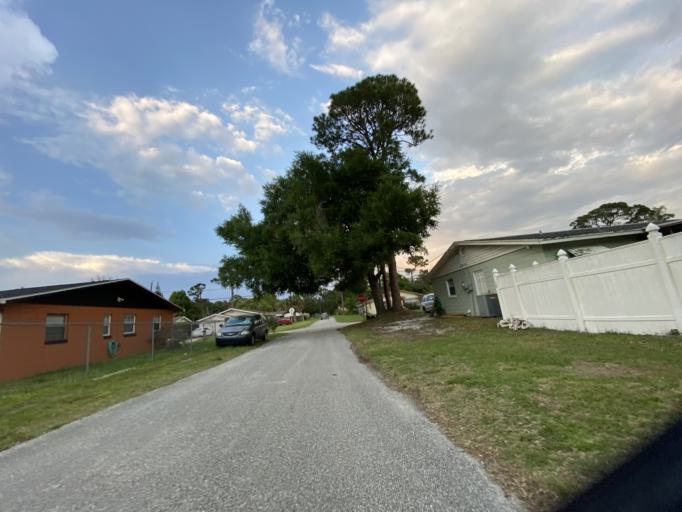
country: US
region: Florida
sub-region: Volusia County
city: Port Orange
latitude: 29.1490
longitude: -80.9977
